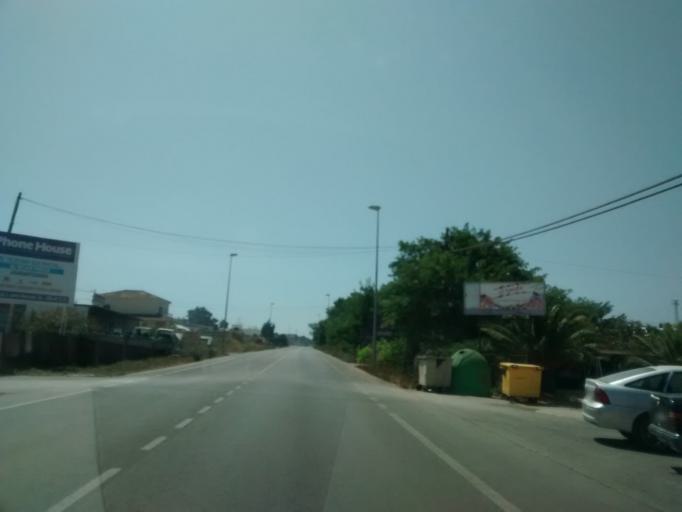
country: ES
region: Andalusia
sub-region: Provincia de Cadiz
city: Conil de la Frontera
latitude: 36.2919
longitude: -6.0751
